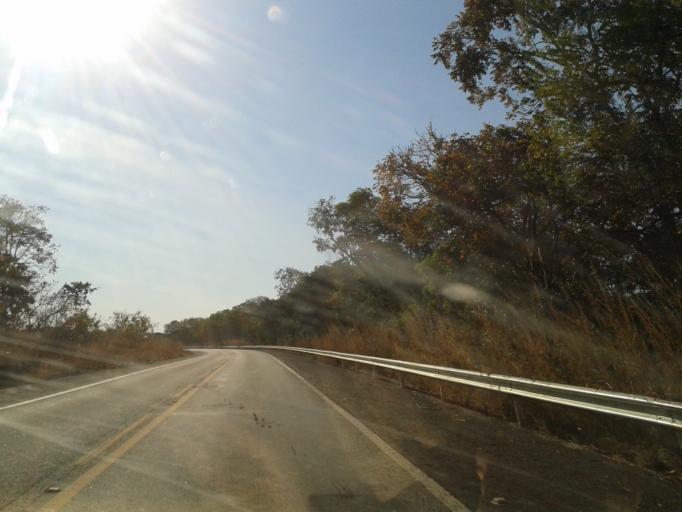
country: BR
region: Goias
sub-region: Mozarlandia
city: Mozarlandia
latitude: -14.9335
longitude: -50.5617
